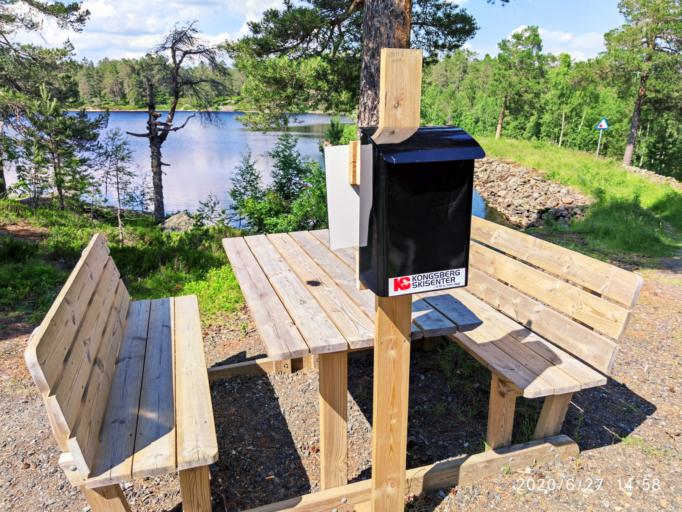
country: NO
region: Buskerud
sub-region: Kongsberg
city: Kongsberg
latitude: 59.6628
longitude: 9.5879
